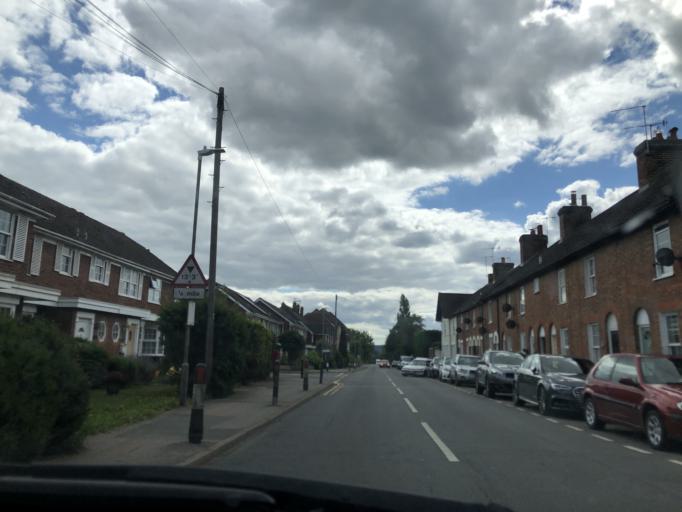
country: GB
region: England
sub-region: Kent
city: Edenbridge
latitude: 51.2121
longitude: 0.0601
